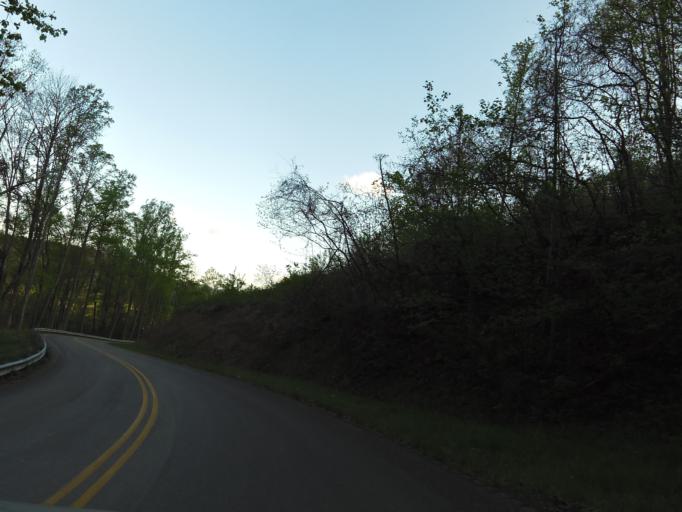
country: US
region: Kentucky
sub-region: Bell County
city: Middlesboro
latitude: 36.6185
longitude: -83.8787
